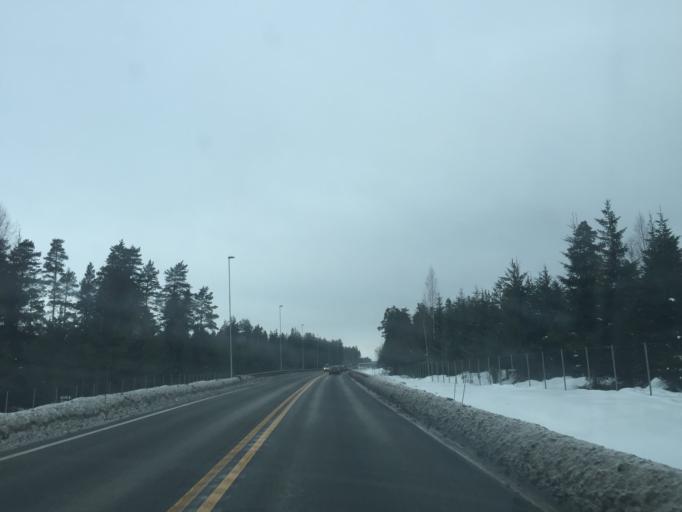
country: NO
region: Hedmark
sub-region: Loten
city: Loten
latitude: 60.7505
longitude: 11.3013
